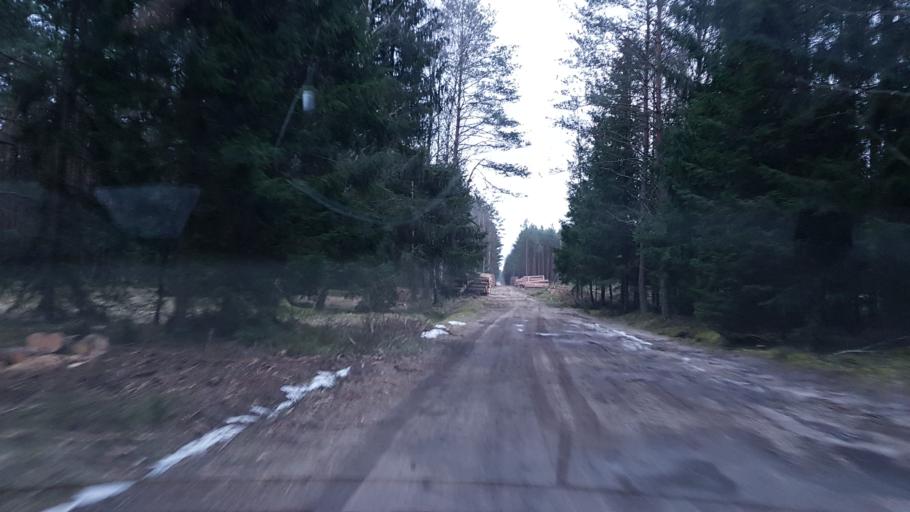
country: PL
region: Greater Poland Voivodeship
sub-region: Powiat zlotowski
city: Sypniewo
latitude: 53.5001
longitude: 16.6773
